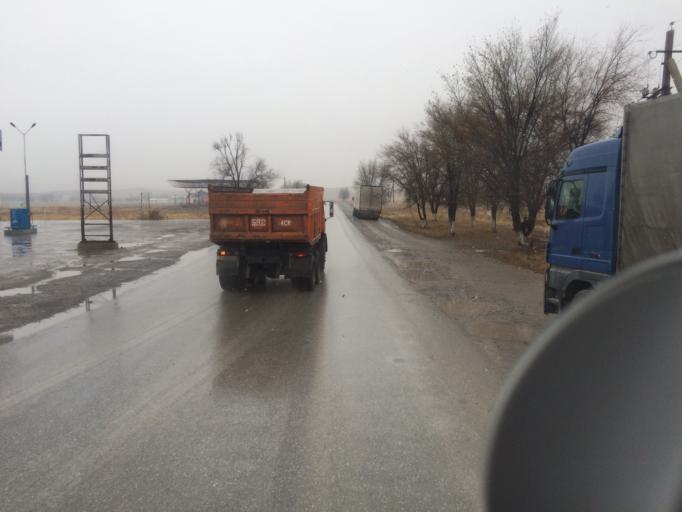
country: KG
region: Chuy
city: Kant
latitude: 43.0019
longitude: 74.8657
